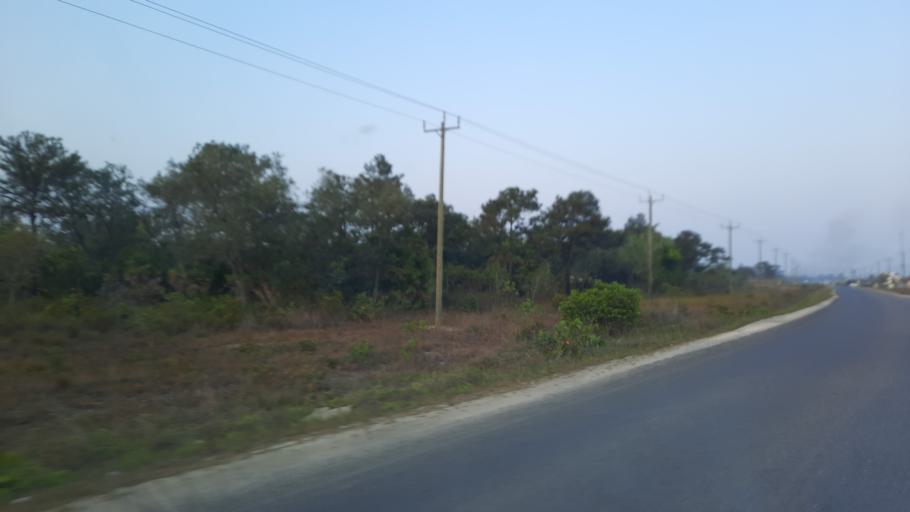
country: BZ
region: Stann Creek
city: Placencia
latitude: 16.5350
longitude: -88.4335
